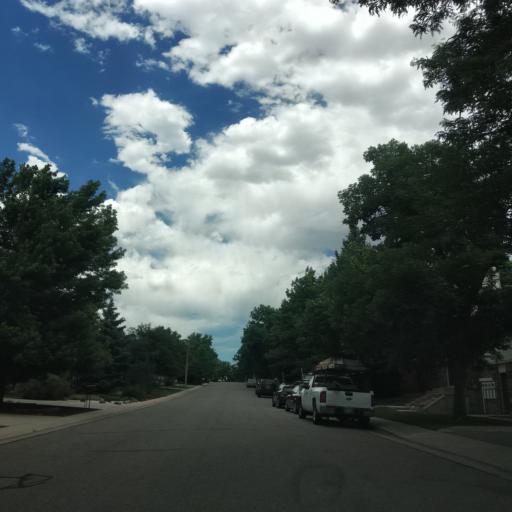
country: US
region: Colorado
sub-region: Jefferson County
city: Lakewood
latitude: 39.6833
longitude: -105.0873
